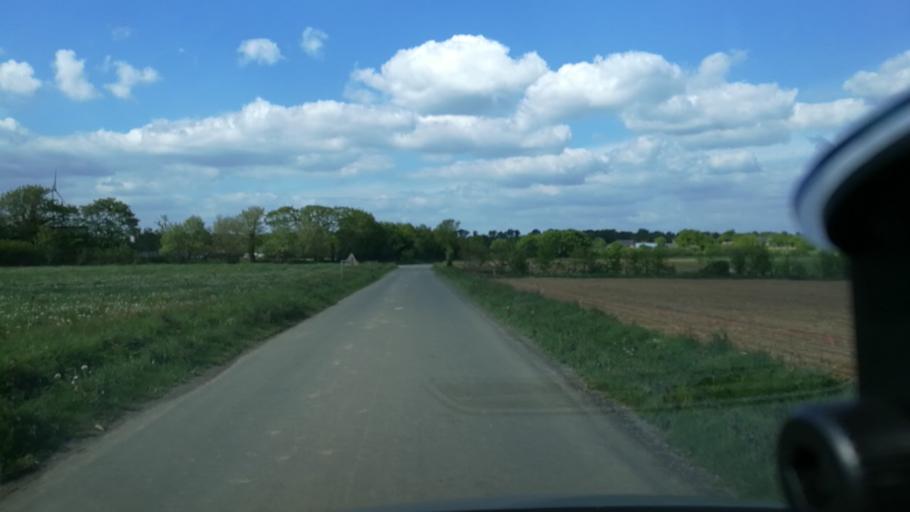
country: FR
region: Brittany
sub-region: Departement d'Ille-et-Vilaine
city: Martigne-Ferchaud
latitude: 47.8668
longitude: -1.3214
